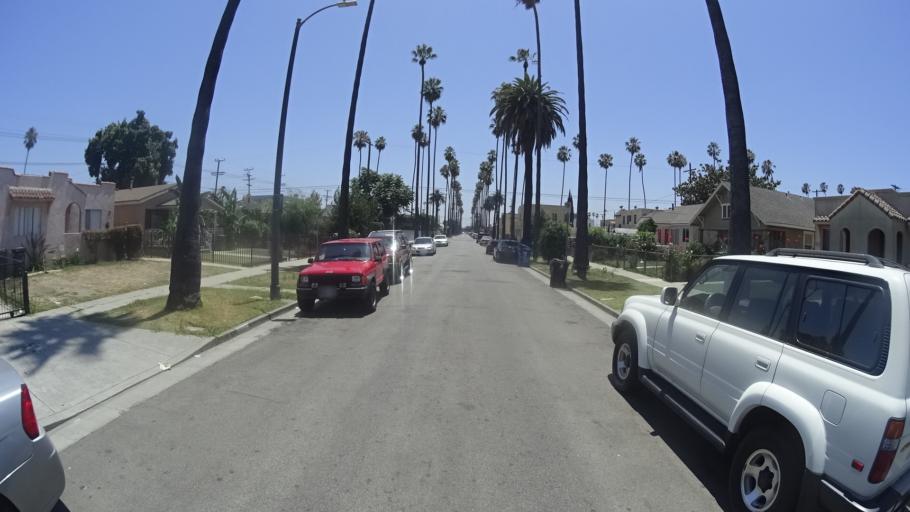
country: US
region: California
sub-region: Los Angeles County
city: View Park-Windsor Hills
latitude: 33.9942
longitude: -118.3101
